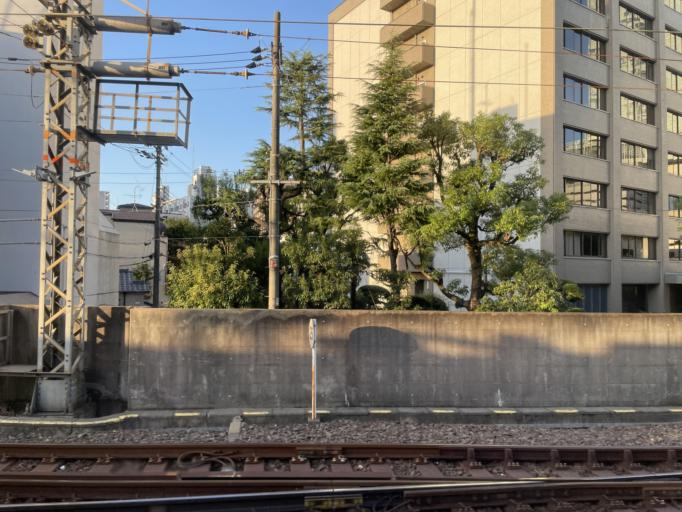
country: JP
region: Osaka
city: Osaka-shi
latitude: 34.6445
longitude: 135.5171
